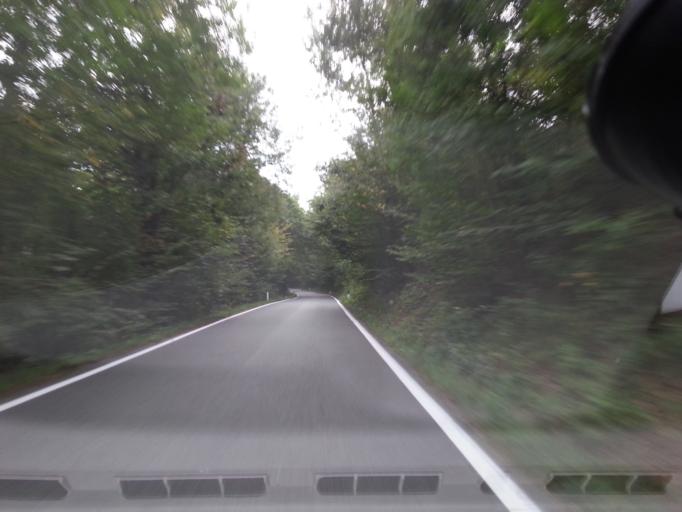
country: IT
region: Piedmont
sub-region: Provincia di Torino
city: Avigliana
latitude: 45.0611
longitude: 7.3802
